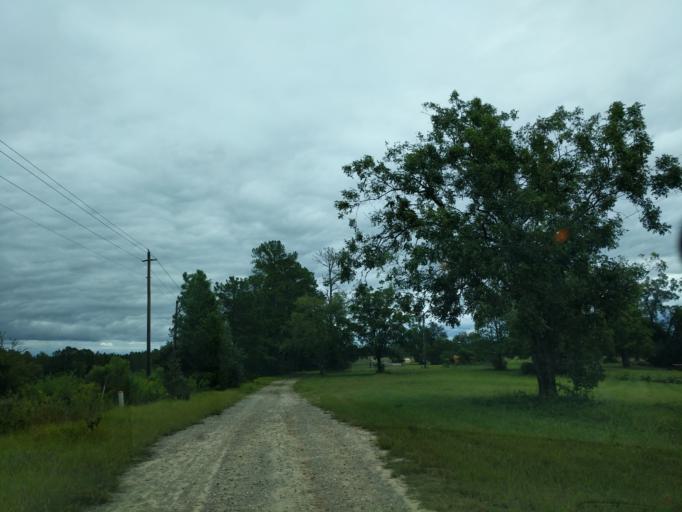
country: US
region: Georgia
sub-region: Wilkes County
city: Washington
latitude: 33.6808
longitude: -82.6335
